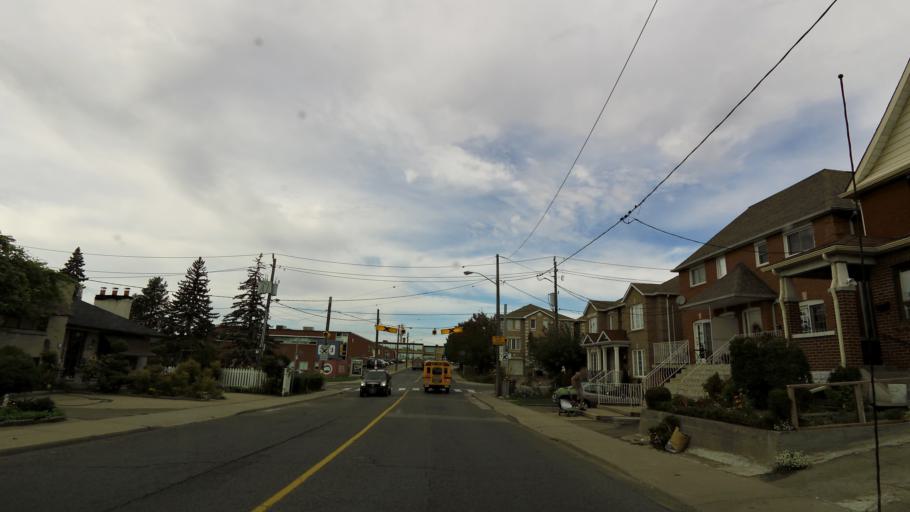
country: CA
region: Ontario
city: Toronto
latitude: 43.6945
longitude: -79.4626
